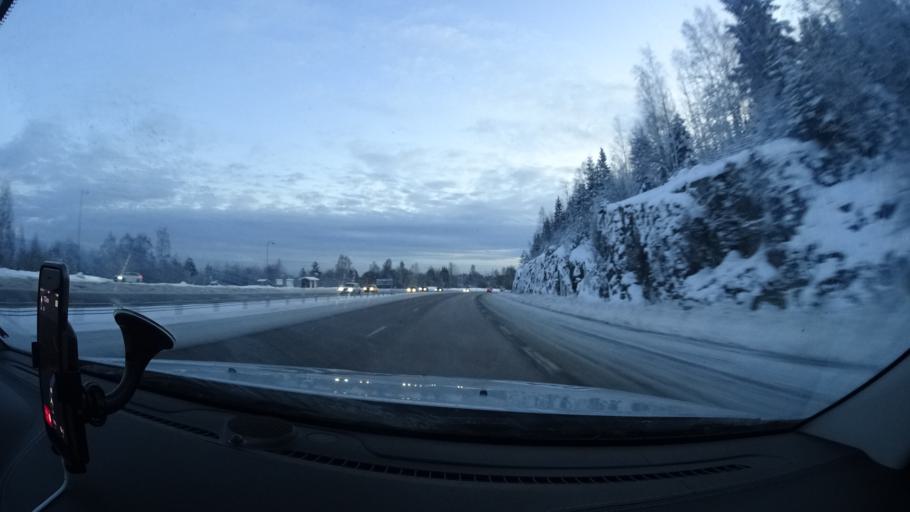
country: SE
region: Vaesternorrland
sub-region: Sundsvalls Kommun
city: Sundsbruk
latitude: 62.4581
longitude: 17.3434
